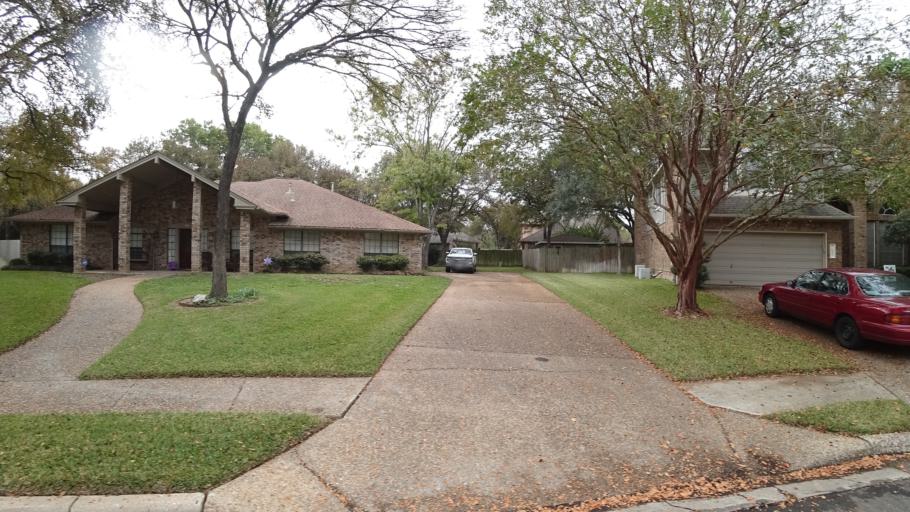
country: US
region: Texas
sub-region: Williamson County
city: Round Rock
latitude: 30.5154
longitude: -97.7037
